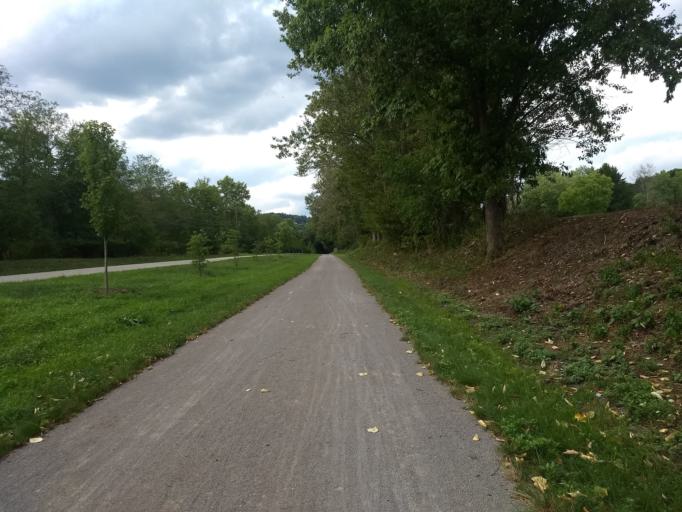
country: US
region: Pennsylvania
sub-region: Armstrong County
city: Freeport
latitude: 40.6584
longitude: -79.6903
